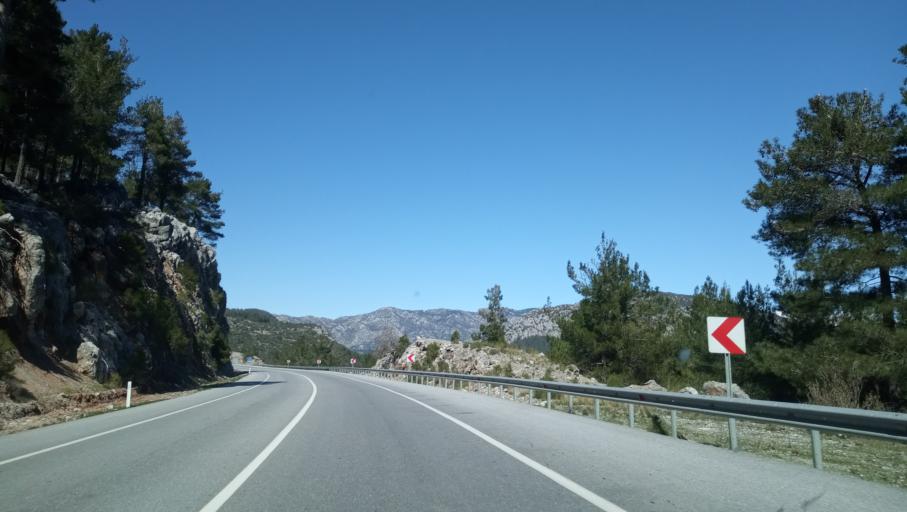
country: TR
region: Antalya
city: Guzelsu
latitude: 36.8405
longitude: 31.7912
